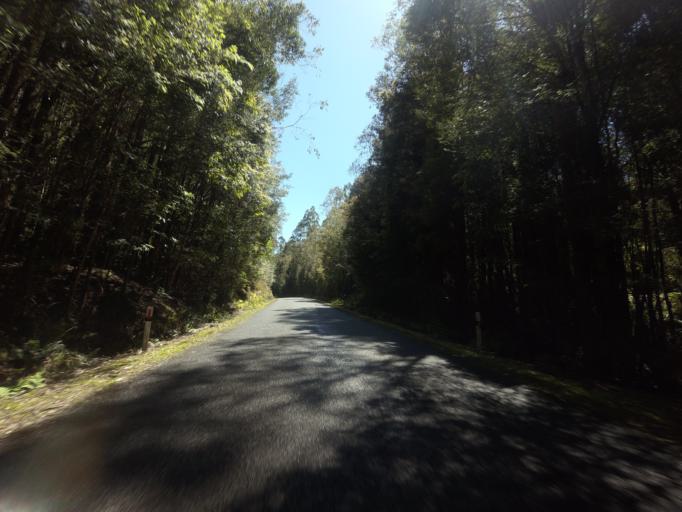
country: AU
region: Tasmania
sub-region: Huon Valley
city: Geeveston
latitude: -42.8255
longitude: 146.3159
